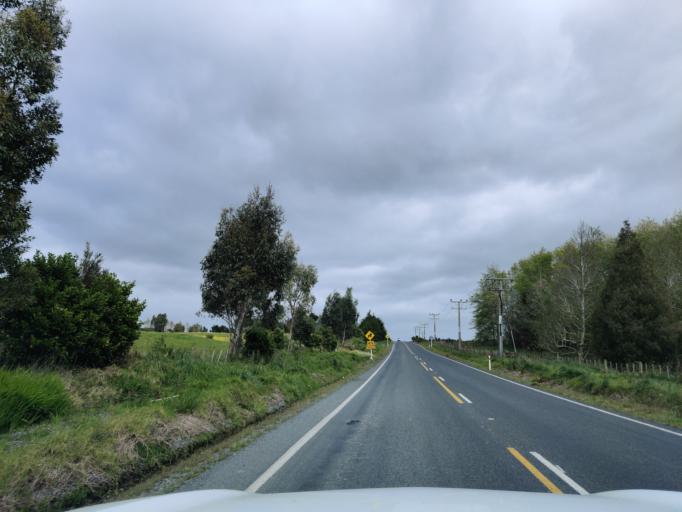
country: NZ
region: Waikato
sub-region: Waikato District
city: Ngaruawahia
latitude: -37.5776
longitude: 175.1383
